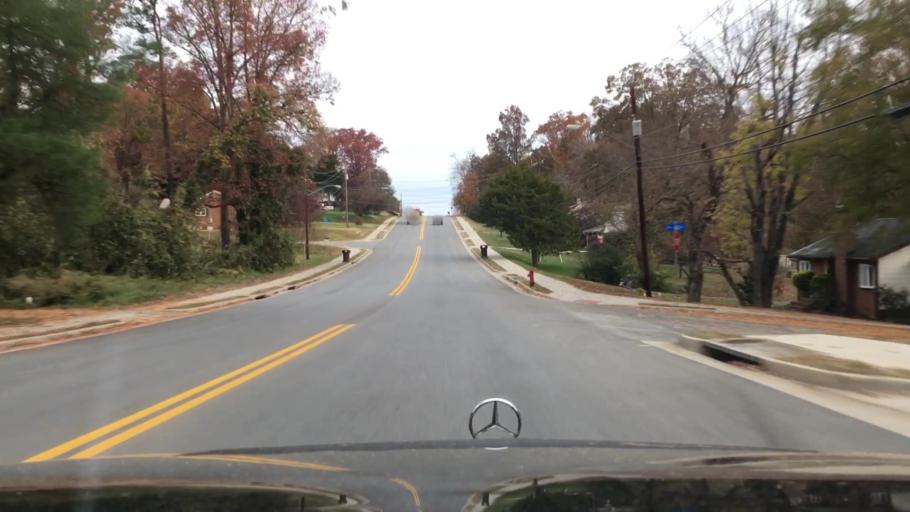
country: US
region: Virginia
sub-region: Campbell County
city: Altavista
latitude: 37.1217
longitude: -79.3033
